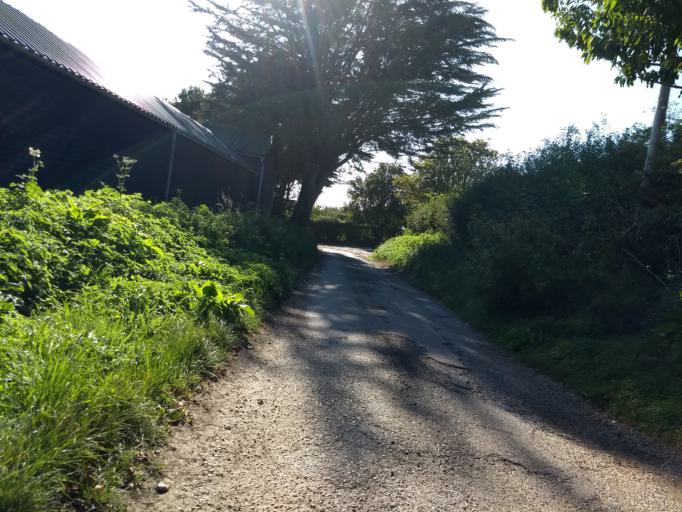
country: GB
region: England
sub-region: Isle of Wight
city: Chale
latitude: 50.6397
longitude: -1.2979
